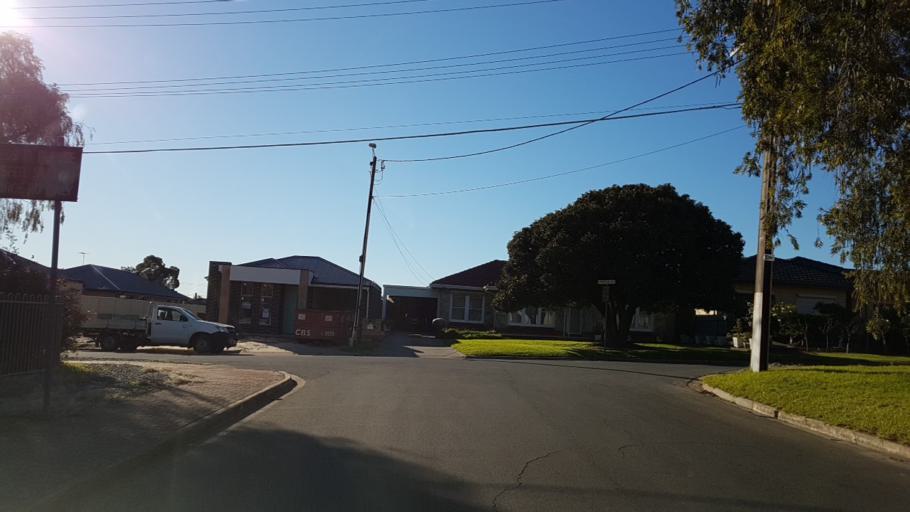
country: AU
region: South Australia
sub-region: Campbelltown
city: Paradise
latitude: -34.8794
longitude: 138.6814
